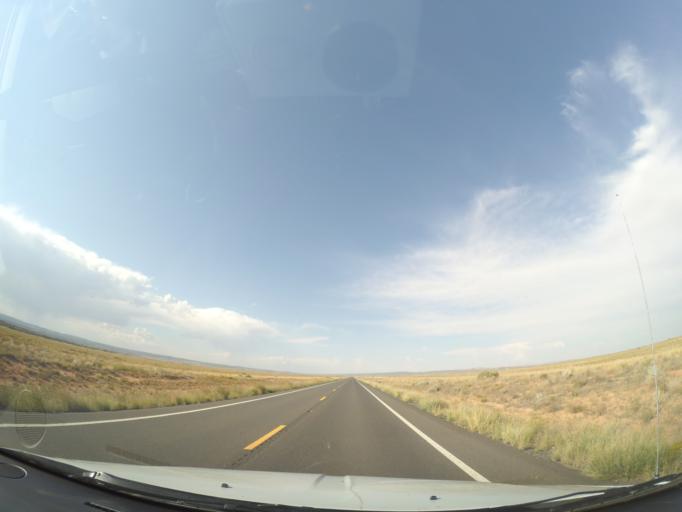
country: US
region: Arizona
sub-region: Coconino County
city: Tuba City
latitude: 36.3632
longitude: -111.4228
